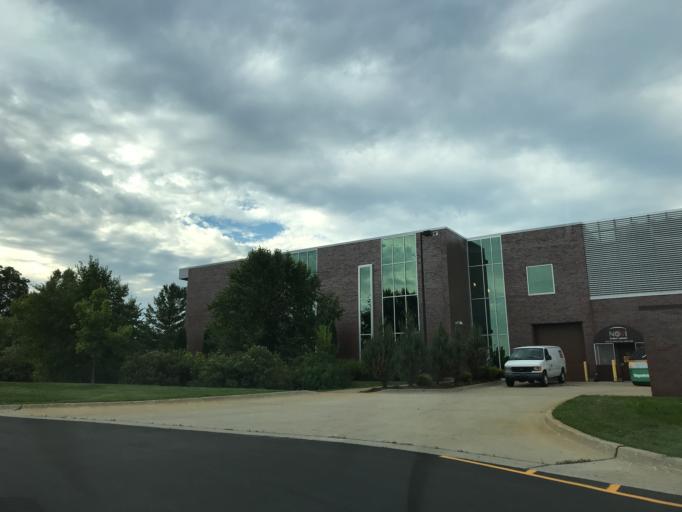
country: US
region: Michigan
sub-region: Oakland County
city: Novi
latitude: 42.4647
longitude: -83.4916
